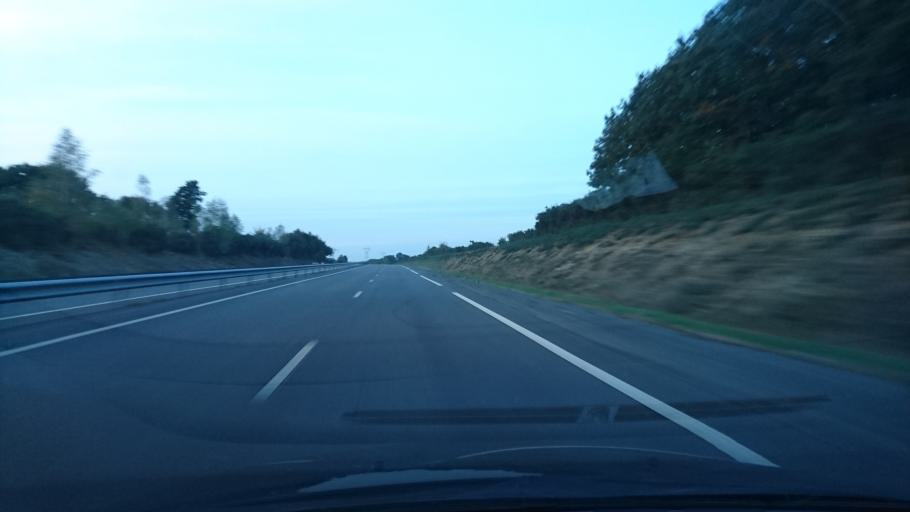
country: FR
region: Brittany
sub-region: Departement d'Ille-et-Vilaine
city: Guichen
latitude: 47.9820
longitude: -1.8138
